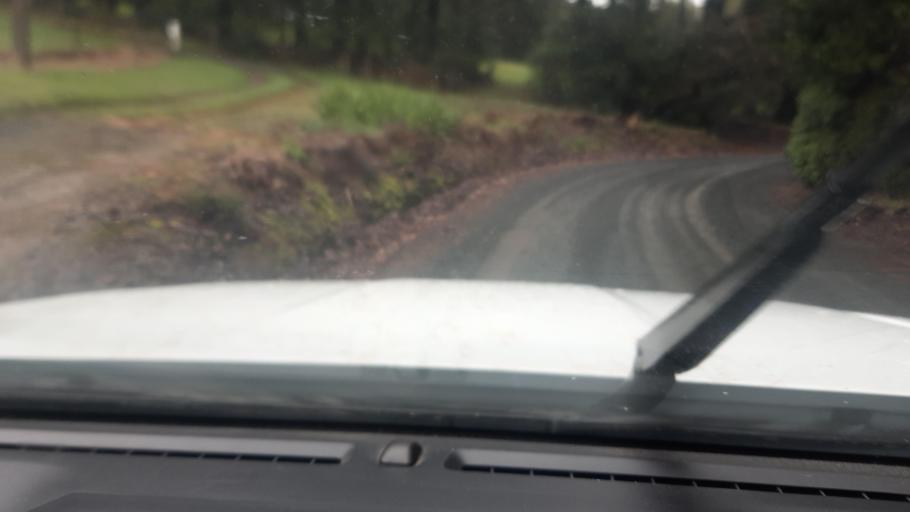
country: NZ
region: Northland
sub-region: Far North District
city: Kaitaia
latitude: -34.9810
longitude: 173.2056
